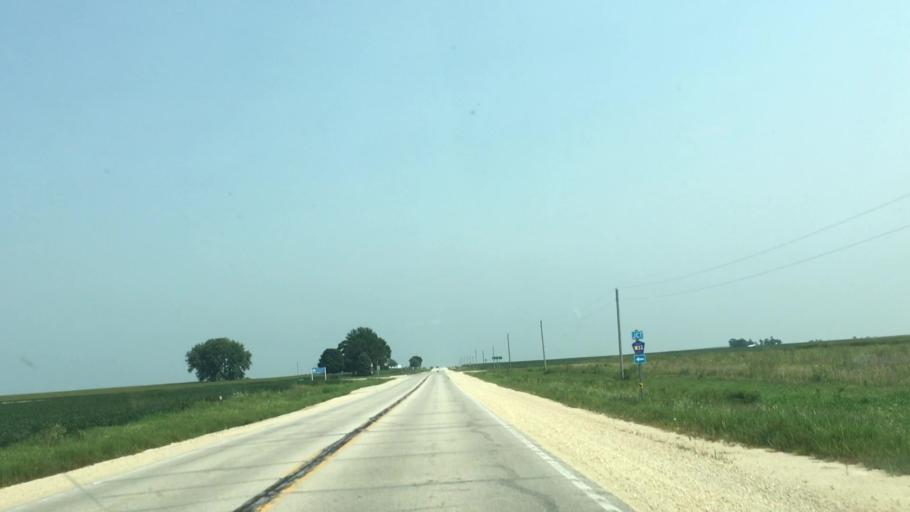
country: US
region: Iowa
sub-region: Fayette County
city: Oelwein
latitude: 42.6873
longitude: -91.8080
